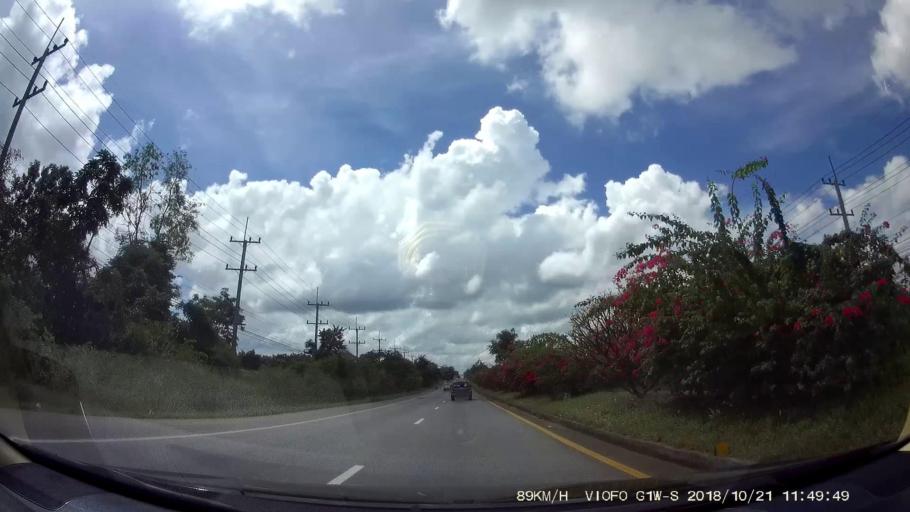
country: TH
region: Chaiyaphum
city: Noen Sa-nga
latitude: 15.6358
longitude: 101.9370
